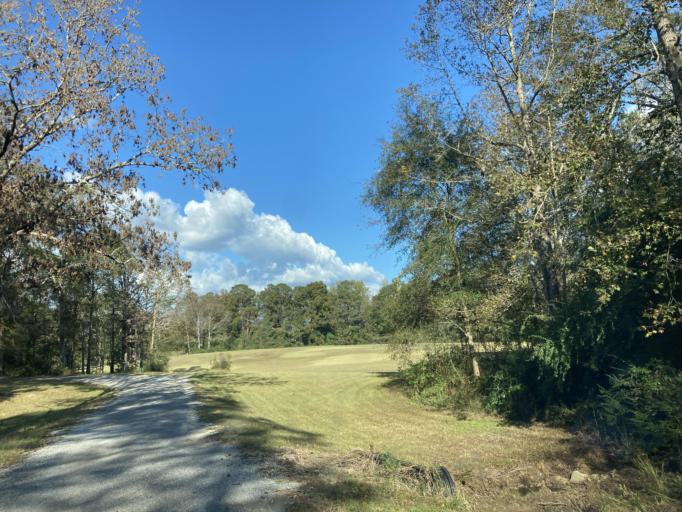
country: US
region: Mississippi
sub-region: Lamar County
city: Sumrall
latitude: 31.4211
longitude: -89.6357
